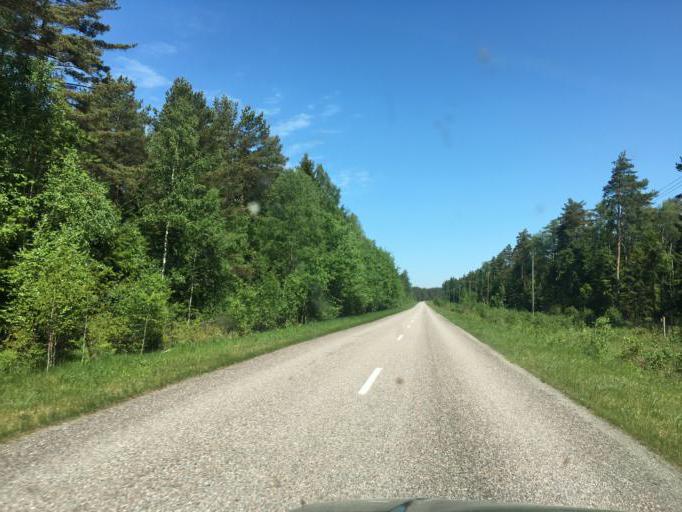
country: LV
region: Ventspils
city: Ventspils
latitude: 57.5024
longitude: 21.6888
